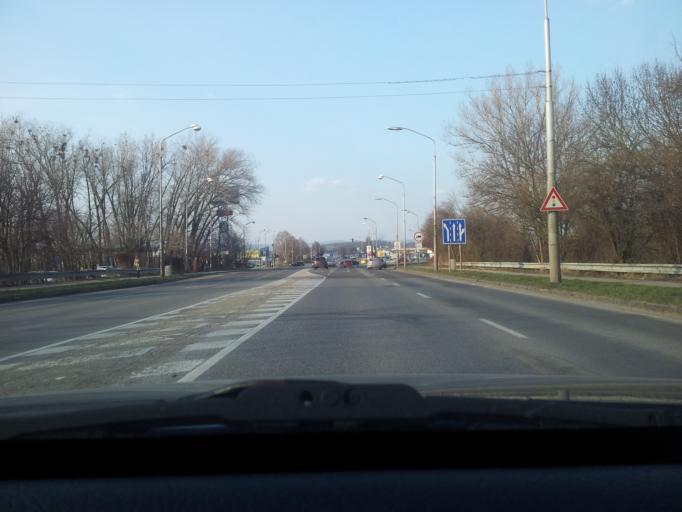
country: SK
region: Nitriansky
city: Levice
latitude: 48.2214
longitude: 18.5991
